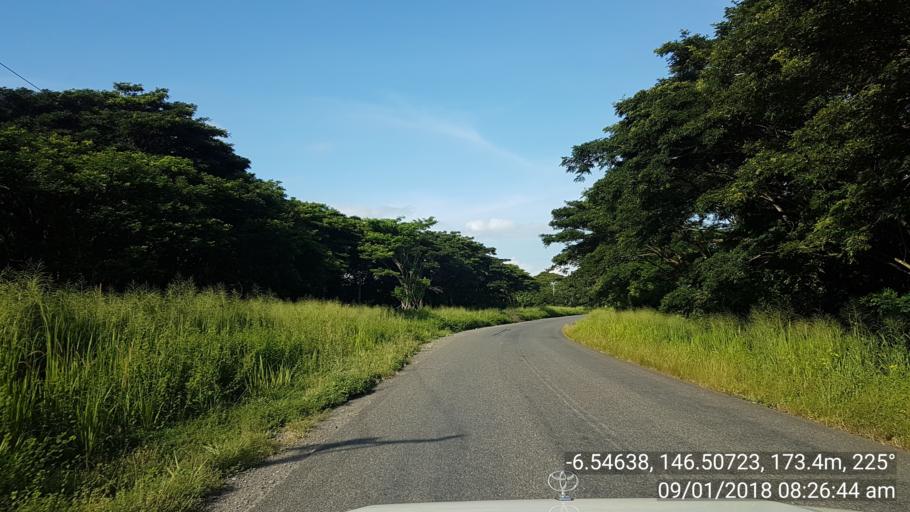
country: PG
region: Morobe
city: Lae
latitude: -6.5464
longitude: 146.5075
